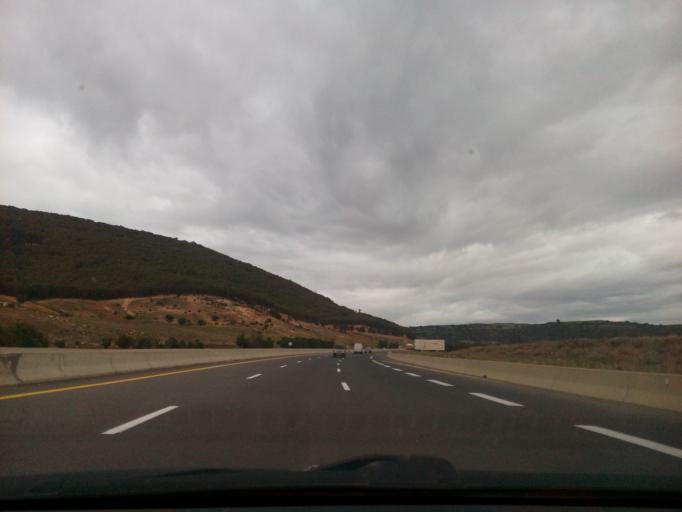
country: DZ
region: Sidi Bel Abbes
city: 'Ain el Berd
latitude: 35.3842
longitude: -0.4985
